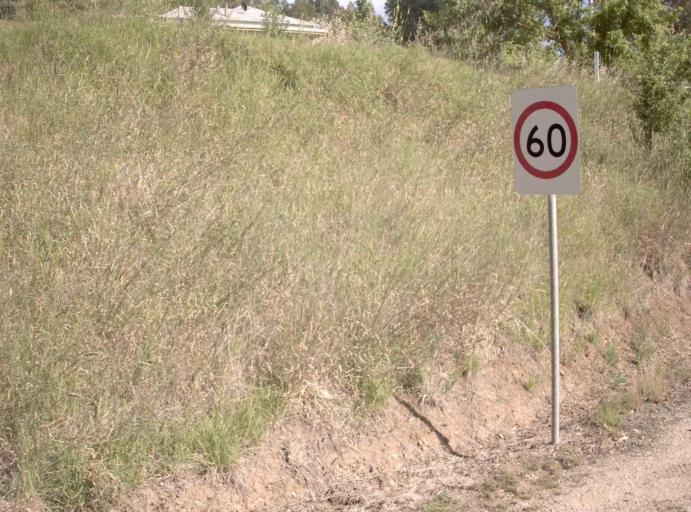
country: AU
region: Victoria
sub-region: East Gippsland
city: Lakes Entrance
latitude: -37.5035
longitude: 148.1704
